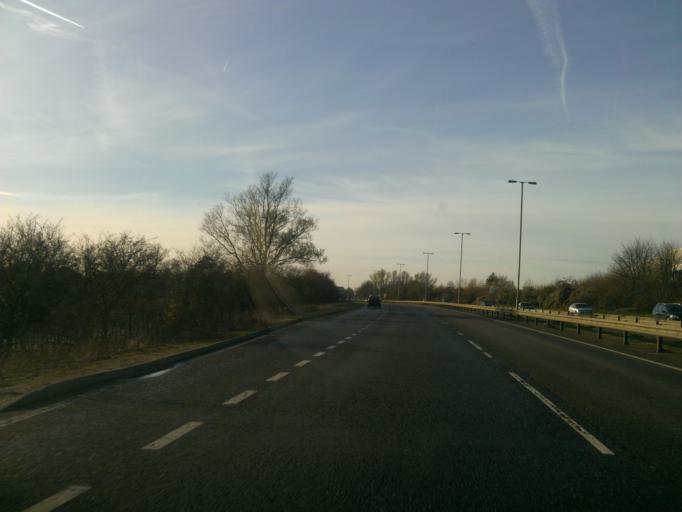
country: GB
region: England
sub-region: Essex
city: Witham
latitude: 51.8124
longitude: 0.6574
